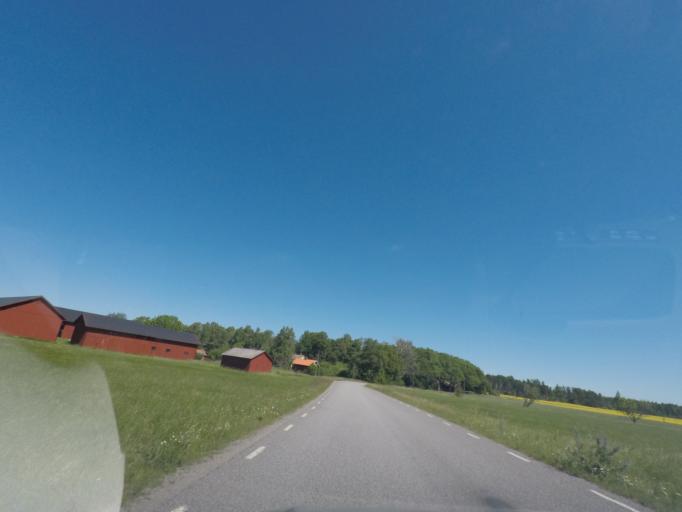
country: SE
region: Uppsala
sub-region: Enkopings Kommun
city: Irsta
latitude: 59.6769
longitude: 16.9181
